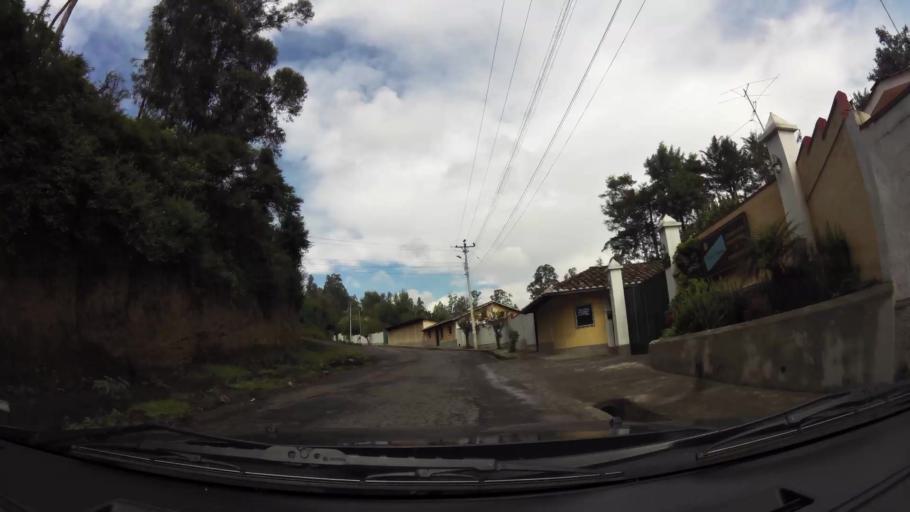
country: EC
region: Pichincha
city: Sangolqui
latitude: -0.3039
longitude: -78.4294
